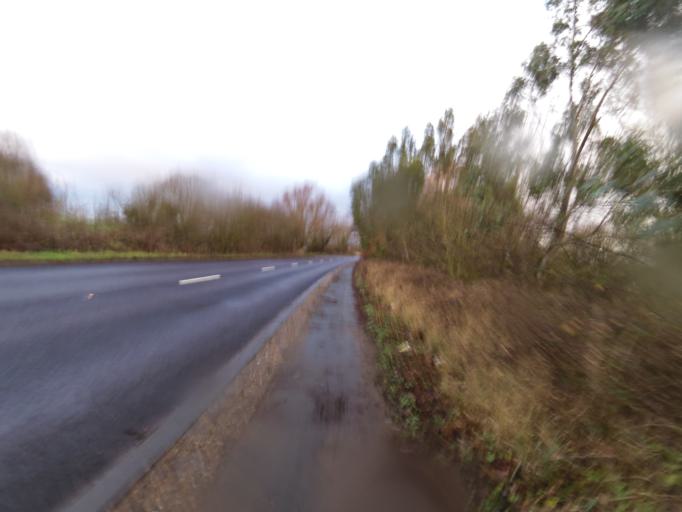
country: GB
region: England
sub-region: Suffolk
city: Needham Market
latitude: 52.1676
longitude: 1.0295
